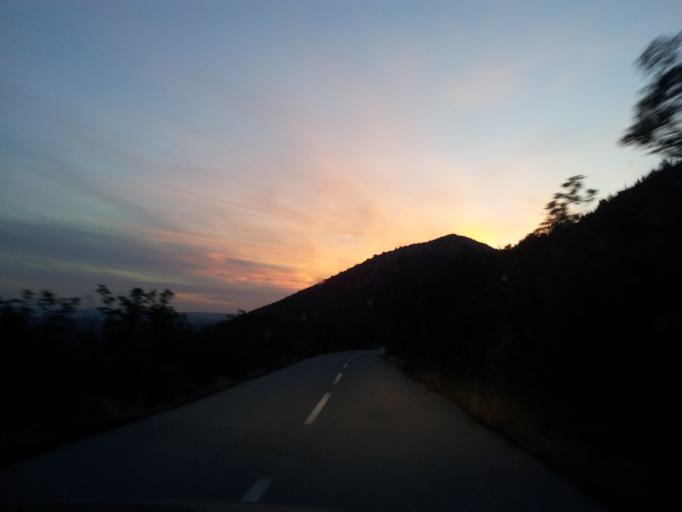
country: HR
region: Zadarska
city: Obrovac
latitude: 44.2369
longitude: 15.6736
